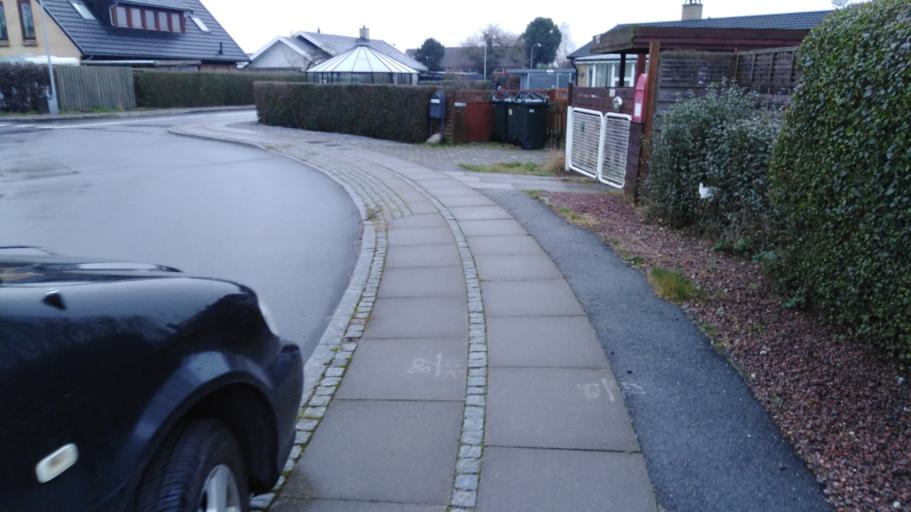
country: DK
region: Capital Region
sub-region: Hvidovre Kommune
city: Hvidovre
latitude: 55.6174
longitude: 12.4865
